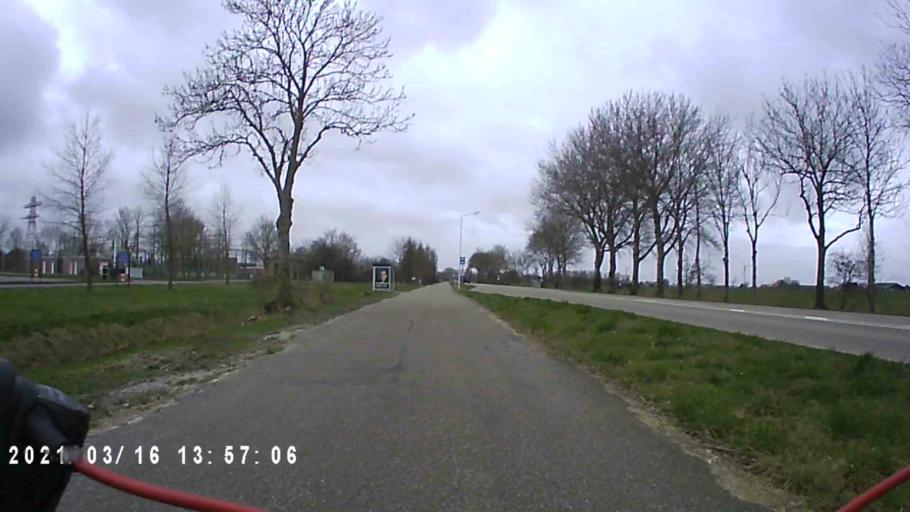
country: NL
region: Friesland
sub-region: Gemeente Franekeradeel
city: Franeker
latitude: 53.1839
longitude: 5.5086
